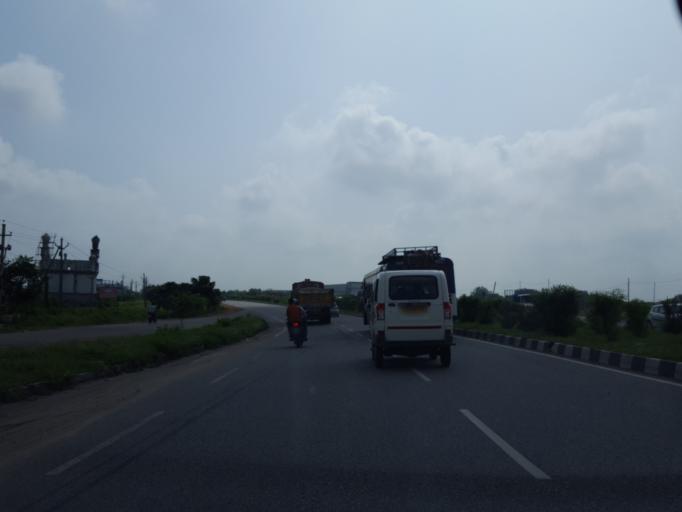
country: IN
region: Telangana
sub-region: Nalgonda
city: Gudur
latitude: 17.2589
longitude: 78.8478
